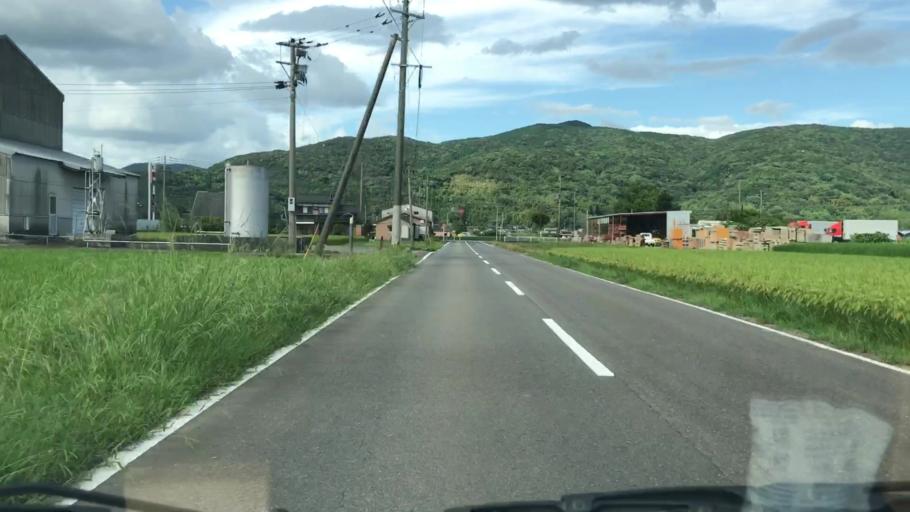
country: JP
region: Saga Prefecture
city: Kashima
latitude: 33.1228
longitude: 130.0725
